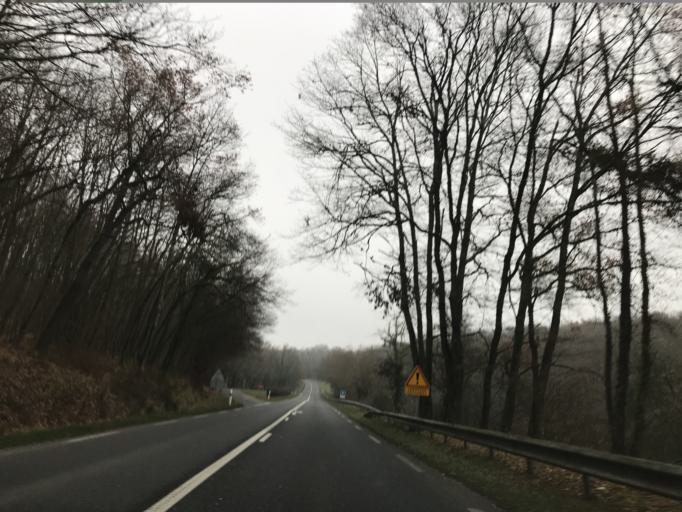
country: FR
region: Auvergne
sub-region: Departement du Puy-de-Dome
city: Orleat
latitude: 45.8272
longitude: 3.4537
